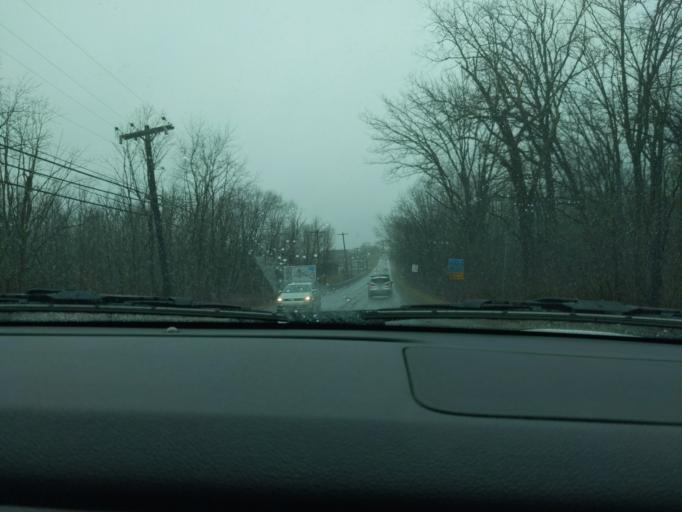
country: US
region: Pennsylvania
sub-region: Bucks County
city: Plumsteadville
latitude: 40.3485
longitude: -75.1632
